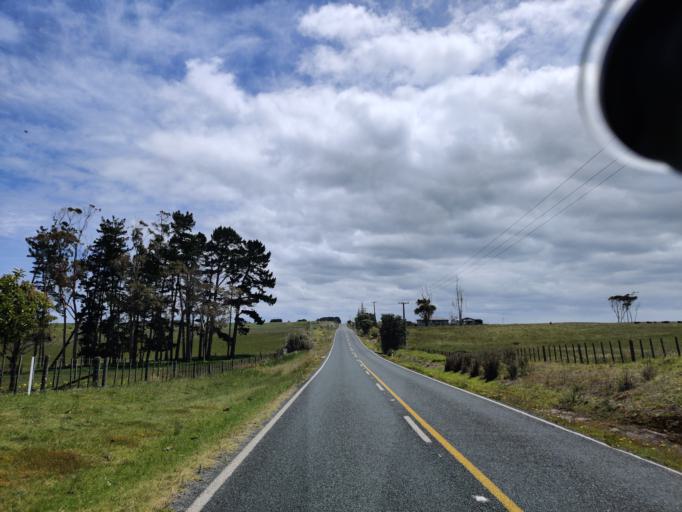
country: NZ
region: Northland
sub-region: Far North District
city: Kaitaia
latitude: -34.7044
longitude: 173.0306
